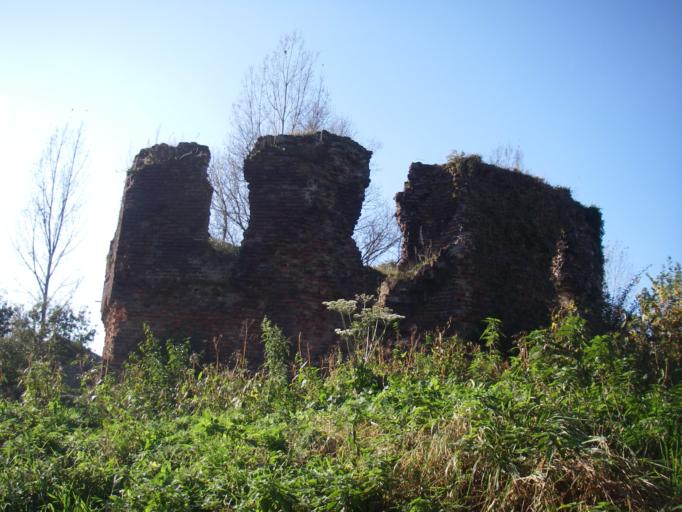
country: NL
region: Limburg
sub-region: Gemeente Roermond
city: Leeuwen
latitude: 51.2320
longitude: 6.0259
